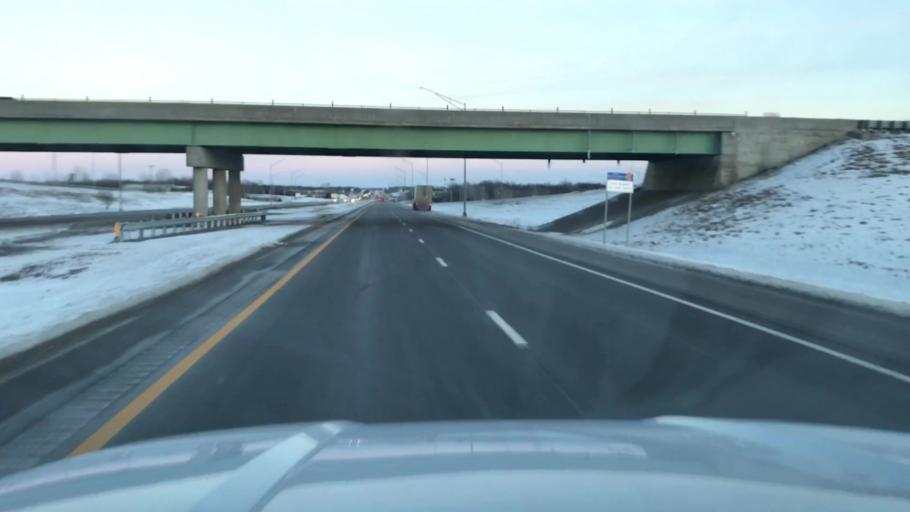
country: US
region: Missouri
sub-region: Clinton County
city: Cameron
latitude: 39.7544
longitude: -94.2349
